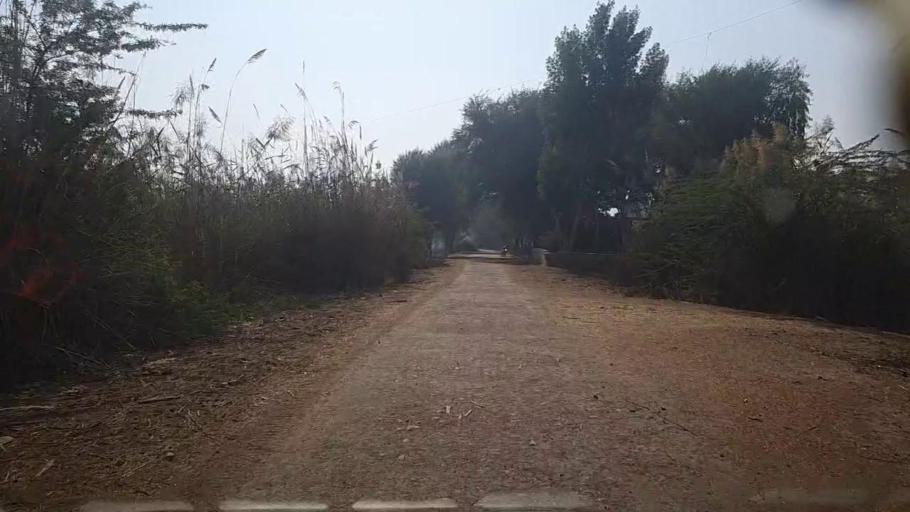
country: PK
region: Sindh
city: Kandiari
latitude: 26.9780
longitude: 68.4694
